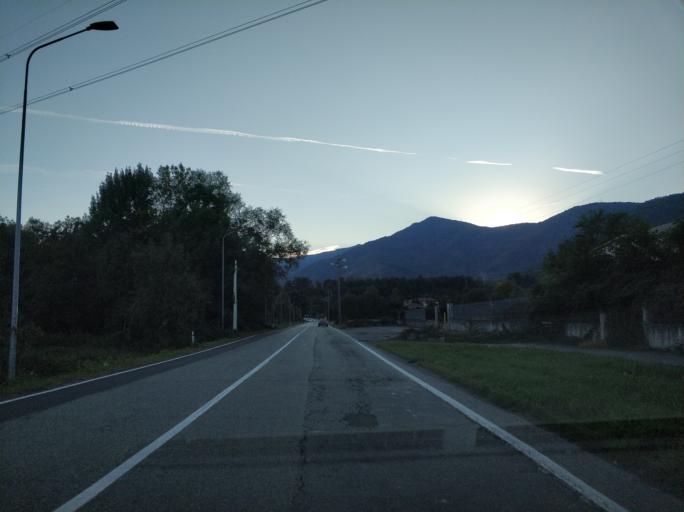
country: IT
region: Piedmont
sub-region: Provincia di Torino
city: Cafasse
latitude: 45.2383
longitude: 7.5306
